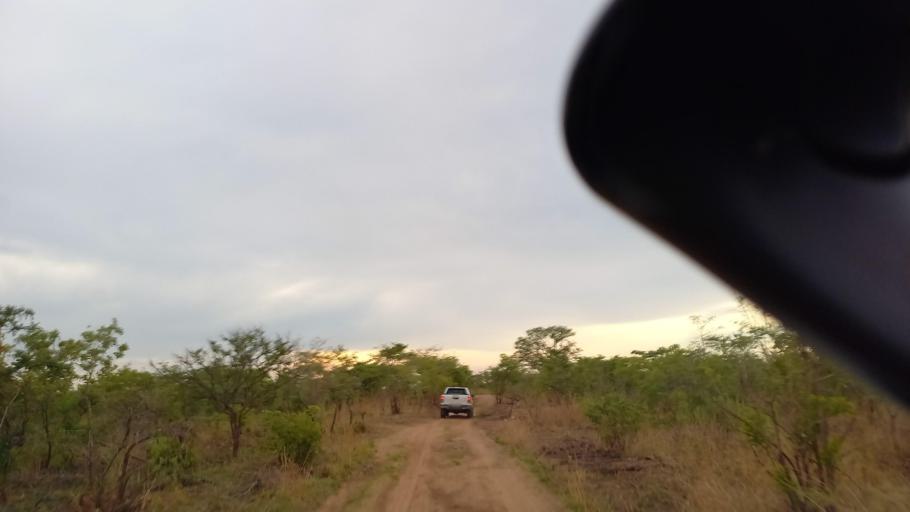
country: ZM
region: Lusaka
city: Kafue
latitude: -16.0481
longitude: 28.3263
